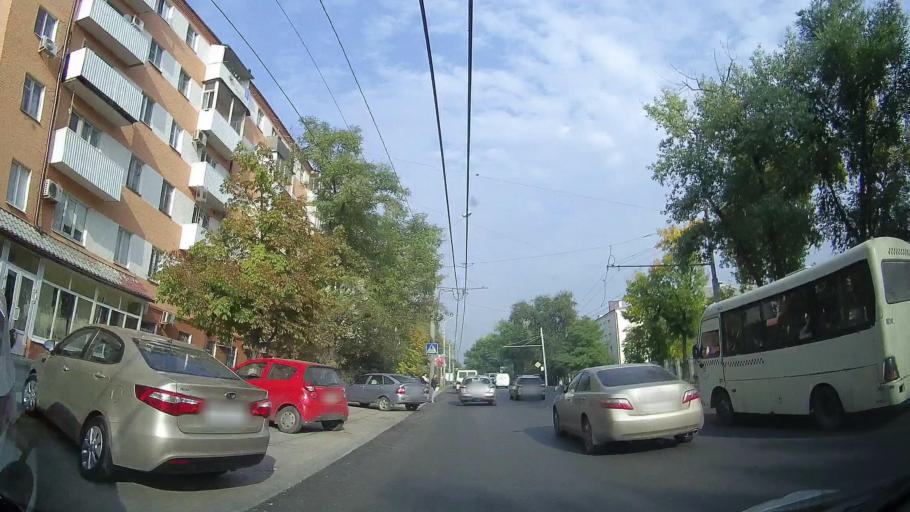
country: RU
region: Rostov
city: Rostov-na-Donu
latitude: 47.2528
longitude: 39.7014
